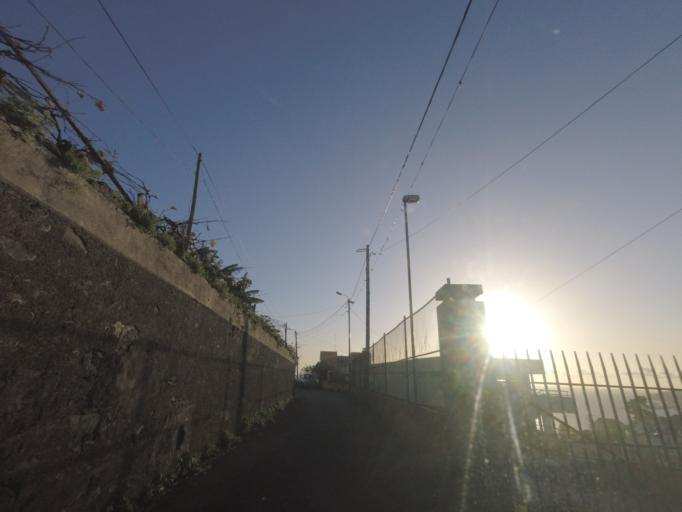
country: PT
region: Madeira
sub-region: Funchal
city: Funchal
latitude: 32.6480
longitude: -16.8868
